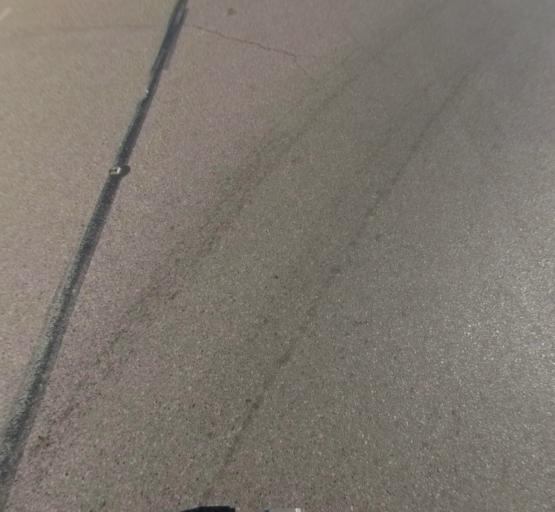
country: US
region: California
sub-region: Fresno County
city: Clovis
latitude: 36.8970
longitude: -119.7908
